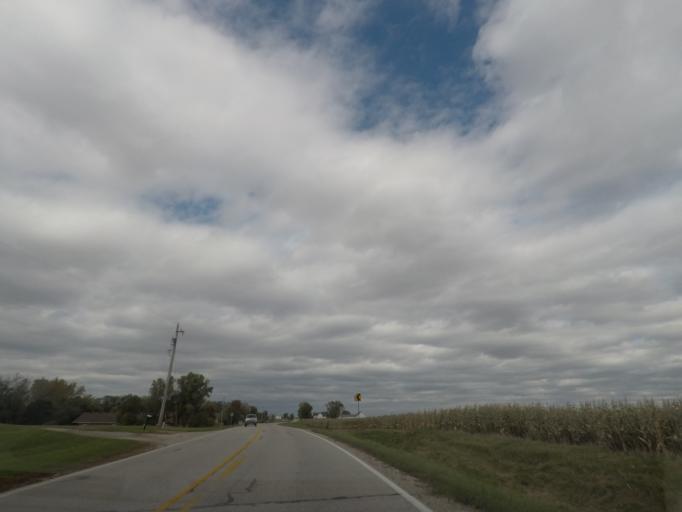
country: US
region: Iowa
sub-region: Story County
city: Huxley
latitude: 41.8389
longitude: -93.5313
